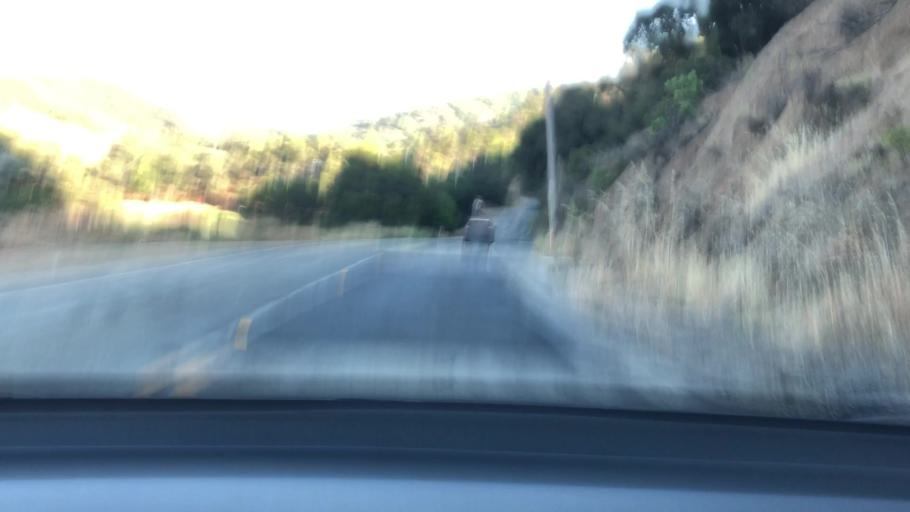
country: US
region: California
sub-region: Santa Clara County
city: Cupertino
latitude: 37.2903
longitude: -122.0815
